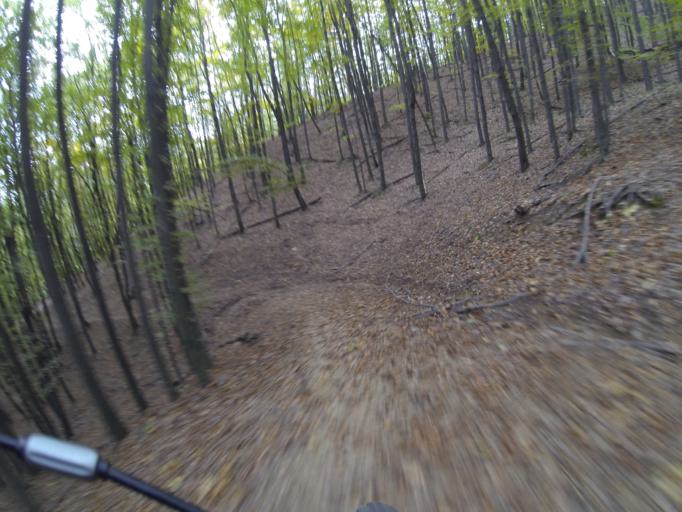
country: RO
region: Gorj
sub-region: Comuna Tismana
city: Sohodol
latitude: 45.0858
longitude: 22.8847
